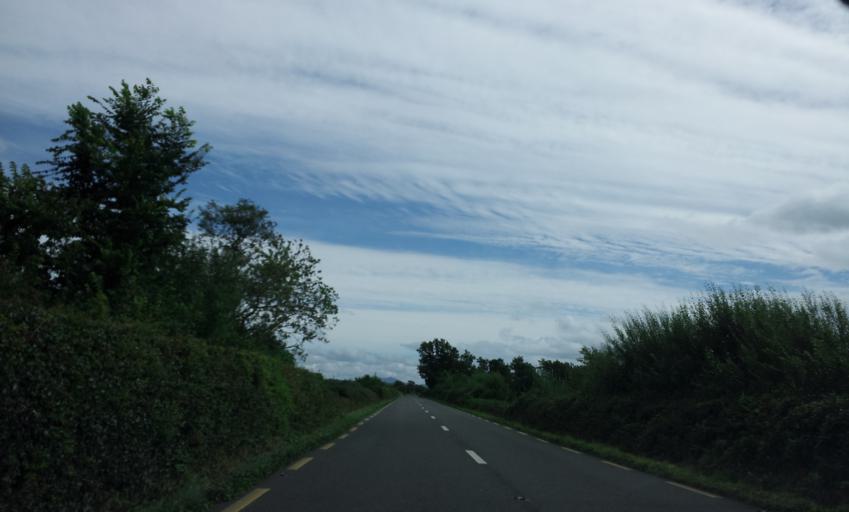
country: IE
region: Munster
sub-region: Ciarrai
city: Killorglin
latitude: 52.0990
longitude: -9.7065
